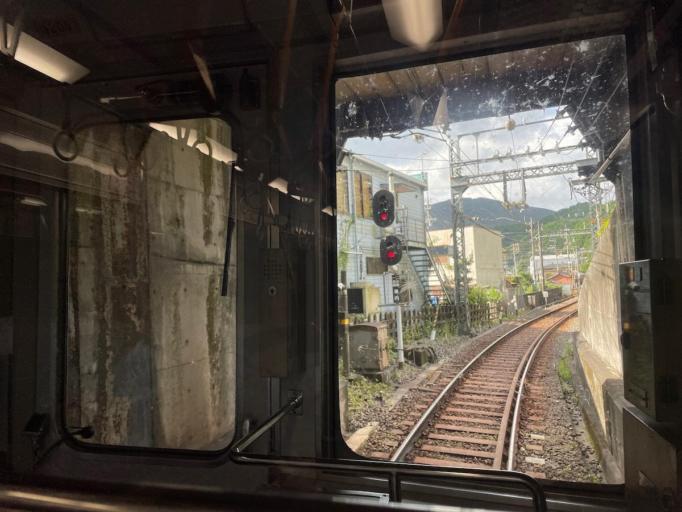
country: JP
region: Mie
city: Toba
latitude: 34.4716
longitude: 136.8449
